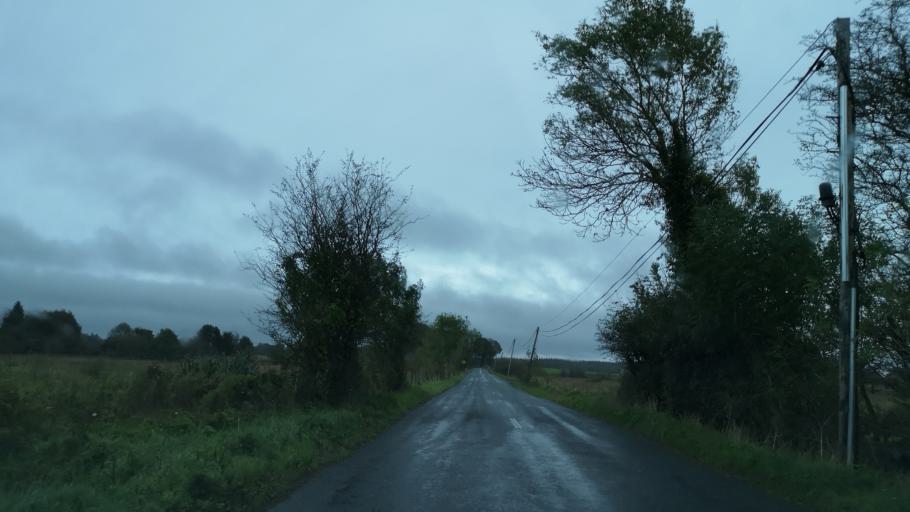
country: IE
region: Connaught
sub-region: Maigh Eo
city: Ballyhaunis
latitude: 53.7744
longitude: -8.7493
